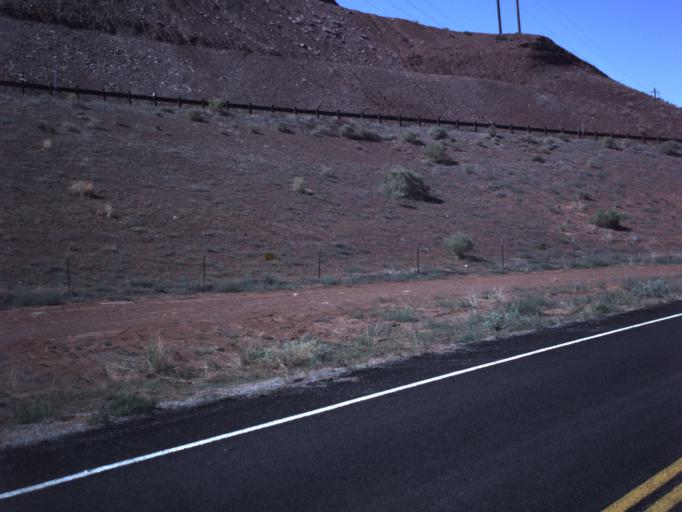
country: US
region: Utah
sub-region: Grand County
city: Moab
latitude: 38.6020
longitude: -109.6039
